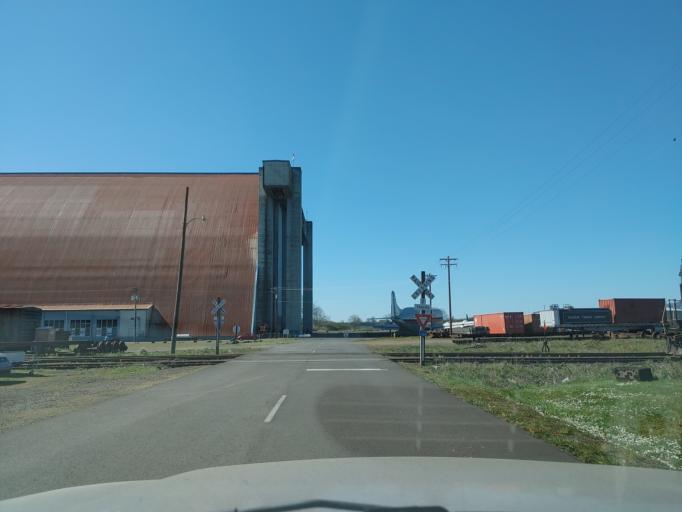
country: US
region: Oregon
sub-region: Tillamook County
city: Tillamook
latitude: 45.4206
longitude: -123.8017
